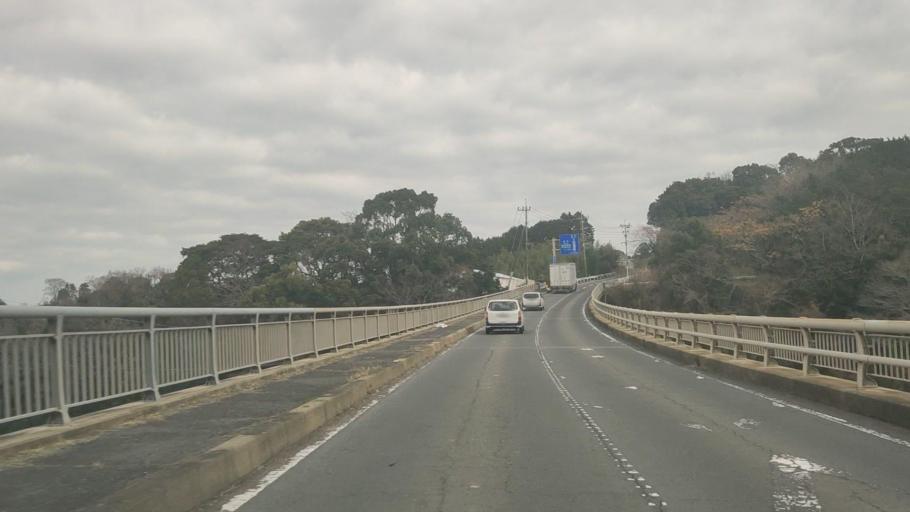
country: JP
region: Nagasaki
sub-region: Isahaya-shi
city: Isahaya
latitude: 32.8146
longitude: 130.1729
